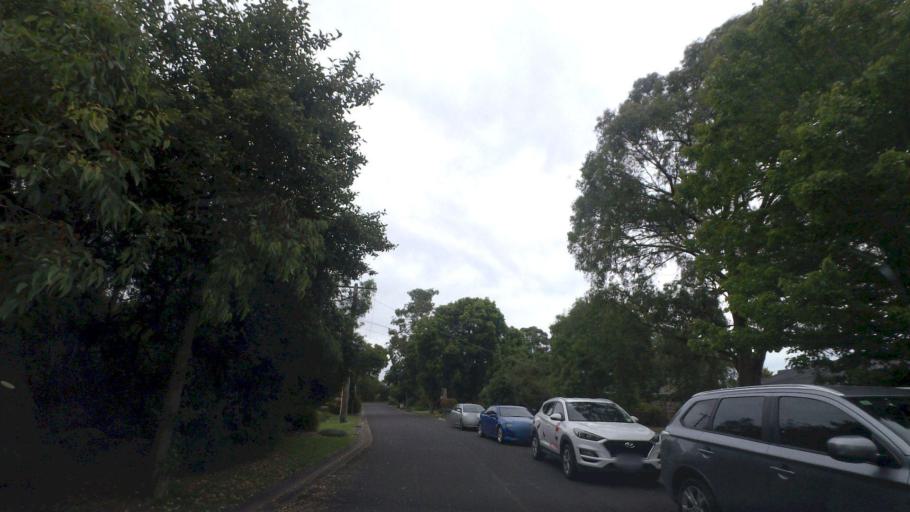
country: AU
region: Victoria
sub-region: Yarra Ranges
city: Kilsyth
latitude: -37.7867
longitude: 145.3335
